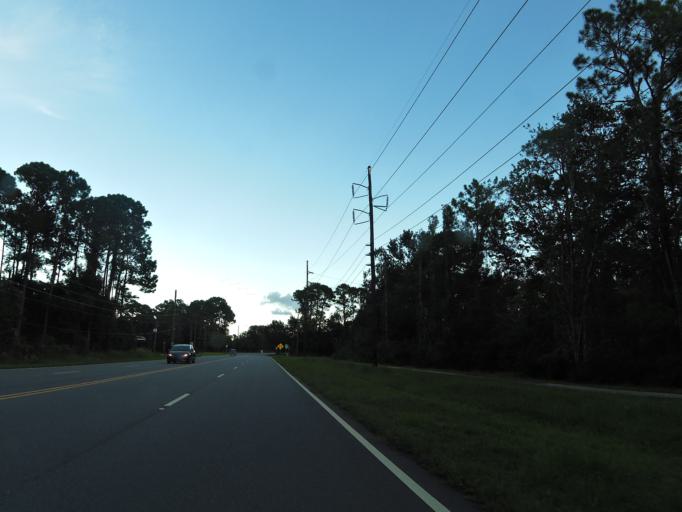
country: US
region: Georgia
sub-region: Camden County
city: St. Marys
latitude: 30.7395
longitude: -81.5488
